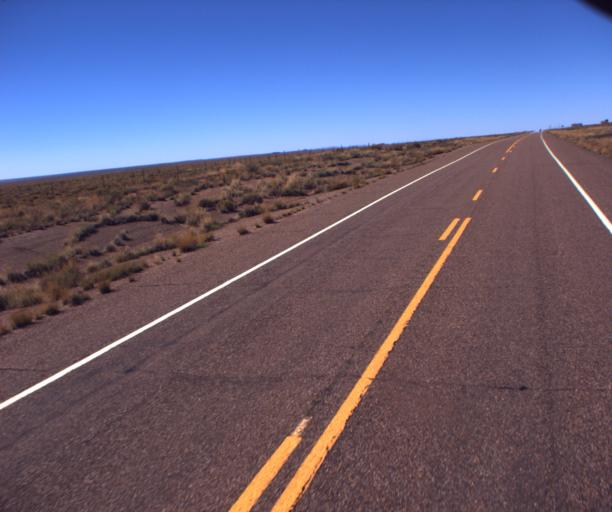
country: US
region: Arizona
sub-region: Navajo County
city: Holbrook
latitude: 34.8561
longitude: -109.9907
